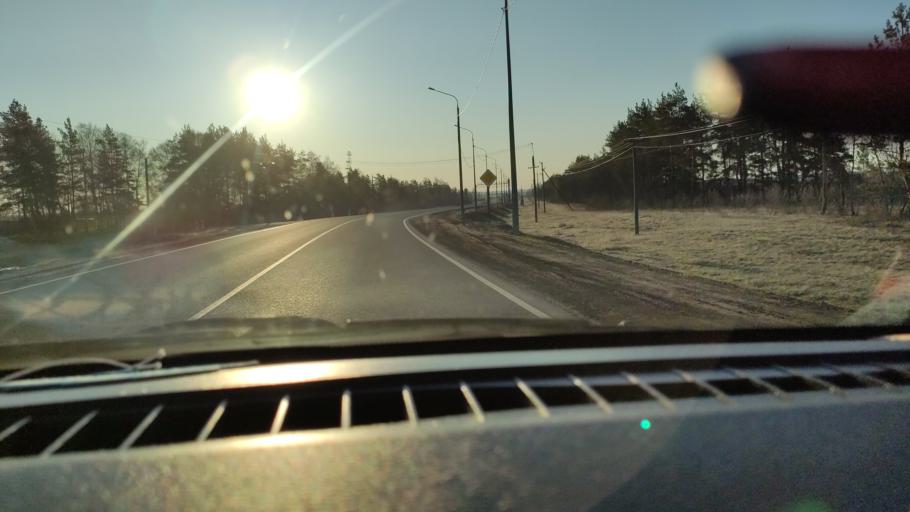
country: RU
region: Saratov
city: Sennoy
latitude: 52.1520
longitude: 46.9659
